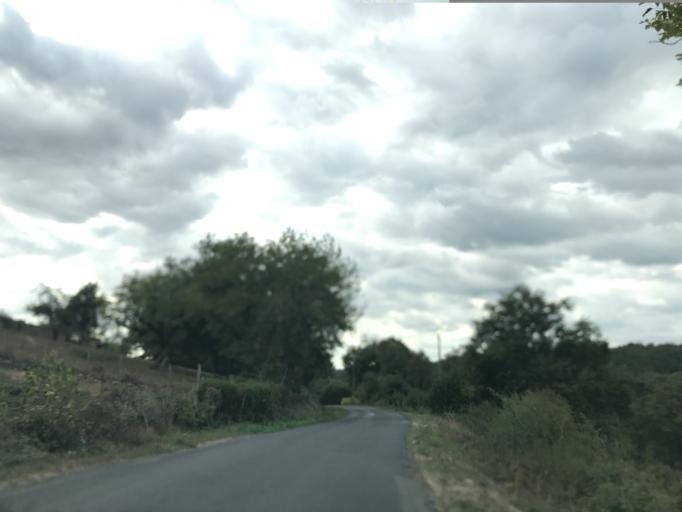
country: FR
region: Auvergne
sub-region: Departement du Puy-de-Dome
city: Courpiere
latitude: 45.7826
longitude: 3.5693
